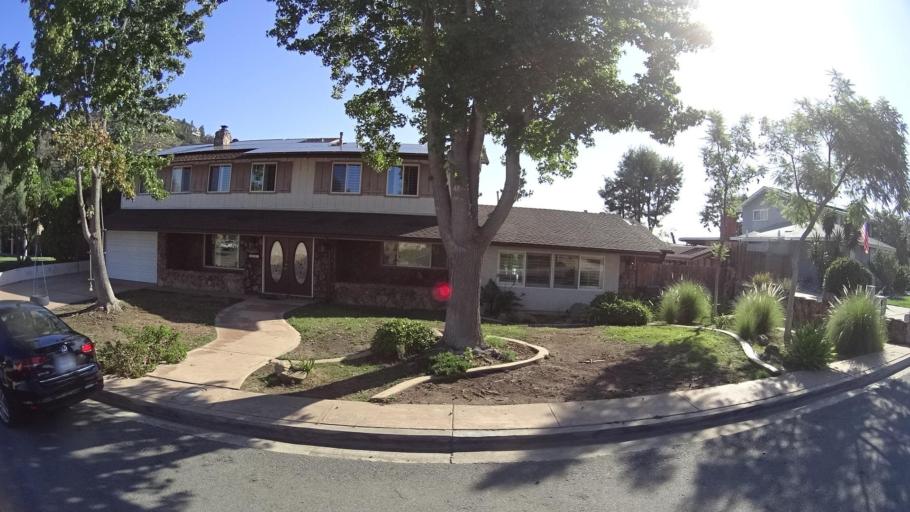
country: US
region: California
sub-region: San Diego County
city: Casa de Oro-Mount Helix
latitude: 32.7621
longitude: -116.9868
